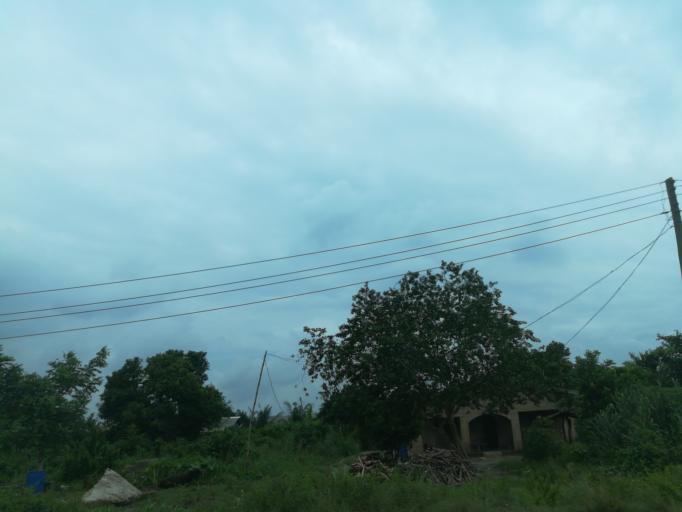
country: NG
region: Lagos
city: Ejirin
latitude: 6.6474
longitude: 3.7677
